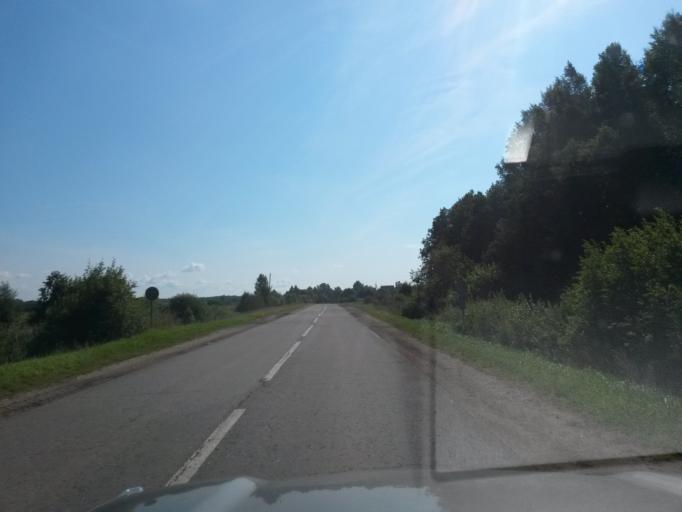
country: RU
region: Jaroslavl
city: Gavrilov-Yam
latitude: 57.3058
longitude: 39.9817
